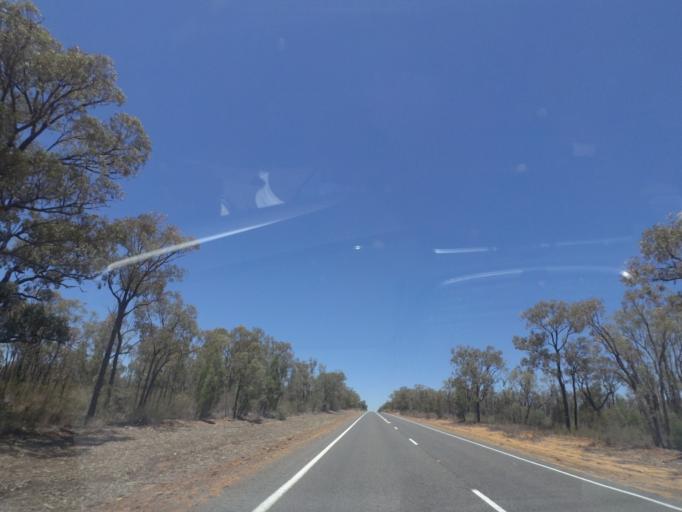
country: AU
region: New South Wales
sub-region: Narrabri
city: Narrabri
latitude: -30.7003
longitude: 149.5348
